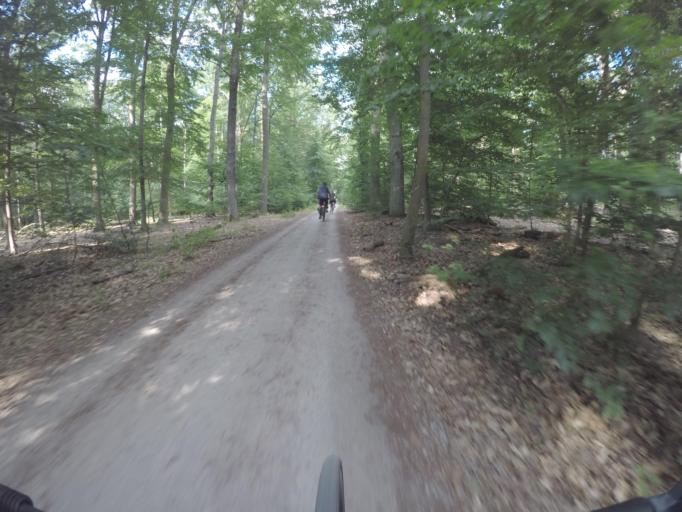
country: DE
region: Berlin
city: Nikolassee
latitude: 52.4142
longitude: 13.1930
